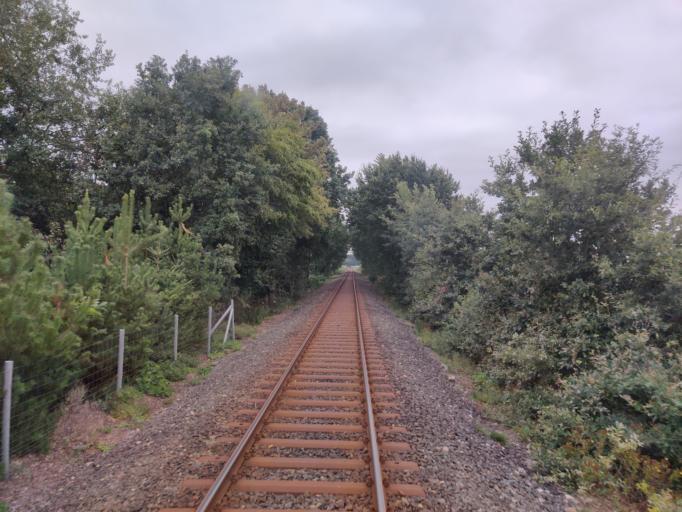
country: DE
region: Lower Saxony
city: Deinste
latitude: 53.5195
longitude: 9.4174
